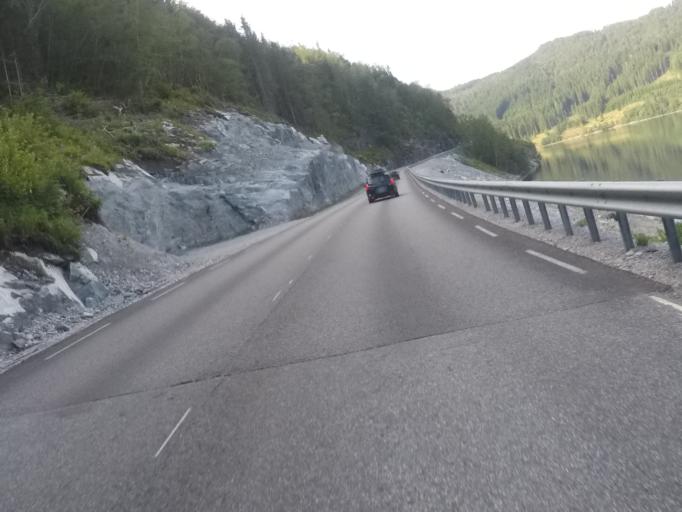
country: NO
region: More og Romsdal
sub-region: Rauma
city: Andalsnes
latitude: 62.5804
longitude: 7.5440
